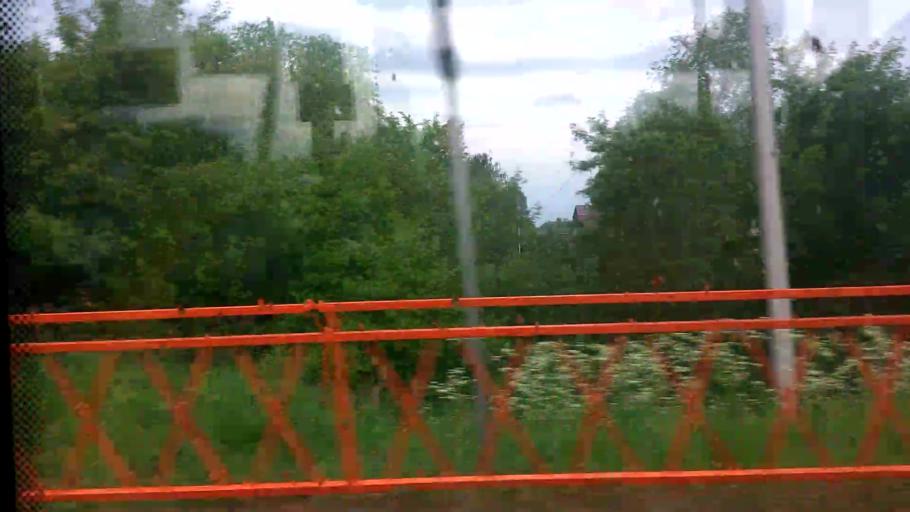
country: RU
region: Moskovskaya
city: Zaraysk
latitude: 54.7551
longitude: 38.8639
